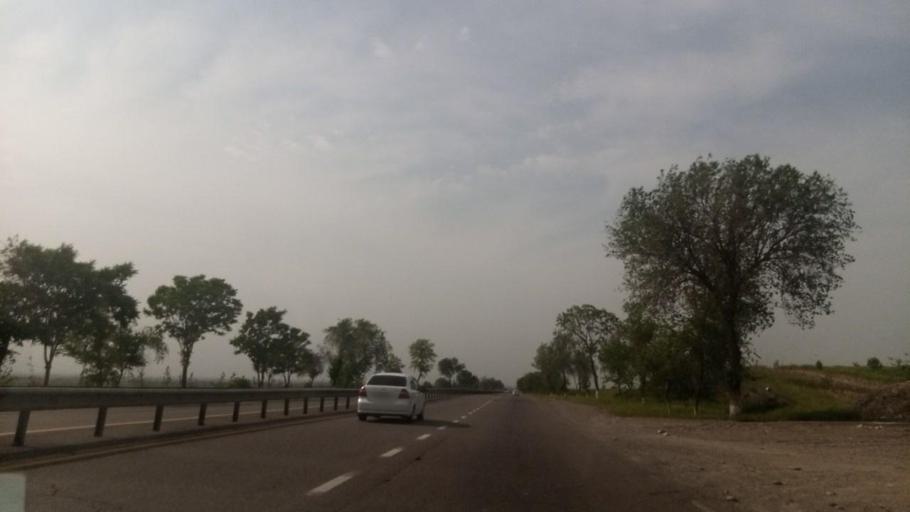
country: UZ
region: Toshkent
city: Tuytepa
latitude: 41.0998
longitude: 69.4566
